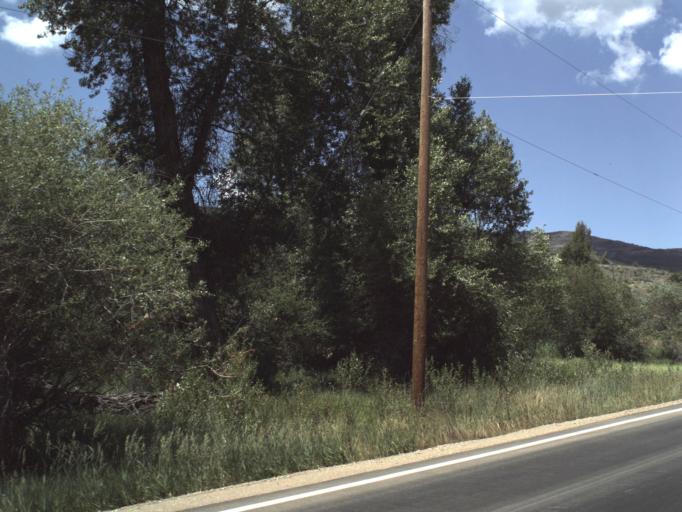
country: US
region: Utah
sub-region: Weber County
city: Wolf Creek
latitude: 41.3035
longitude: -111.6181
